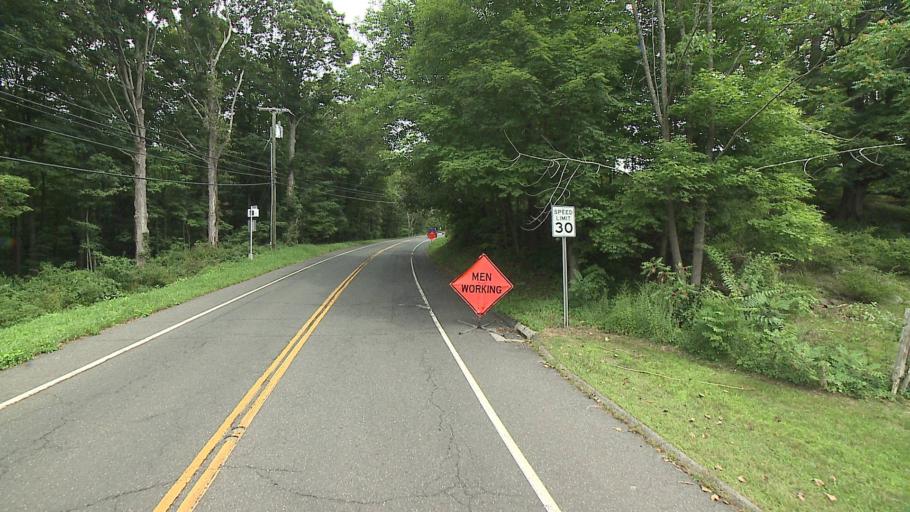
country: US
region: Connecticut
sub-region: Litchfield County
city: Woodbury
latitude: 41.5620
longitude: -73.3016
